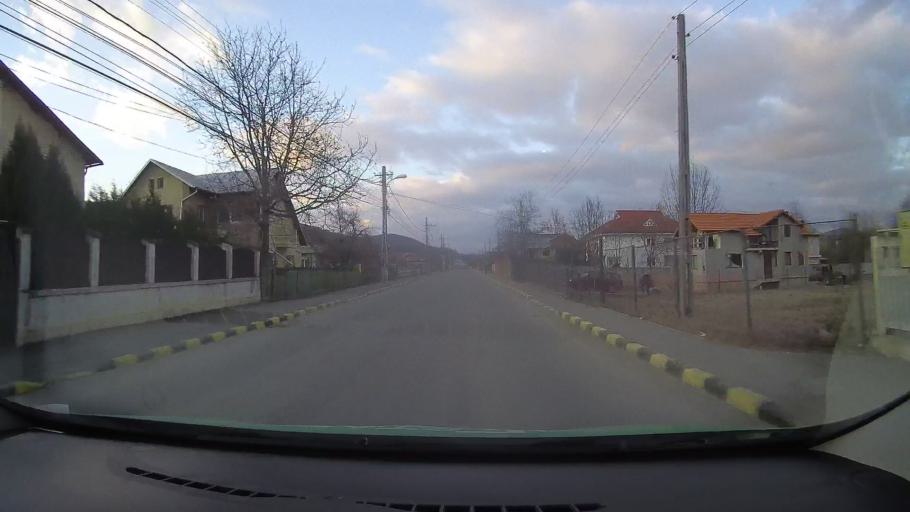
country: RO
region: Dambovita
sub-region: Municipiul Moreni
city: Moreni
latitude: 44.9871
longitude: 25.6384
